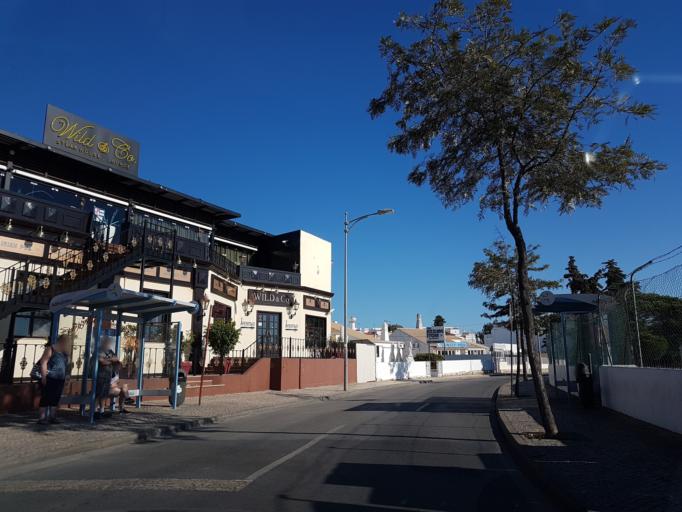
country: PT
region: Faro
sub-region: Albufeira
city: Albufeira
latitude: 37.0890
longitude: -8.2272
